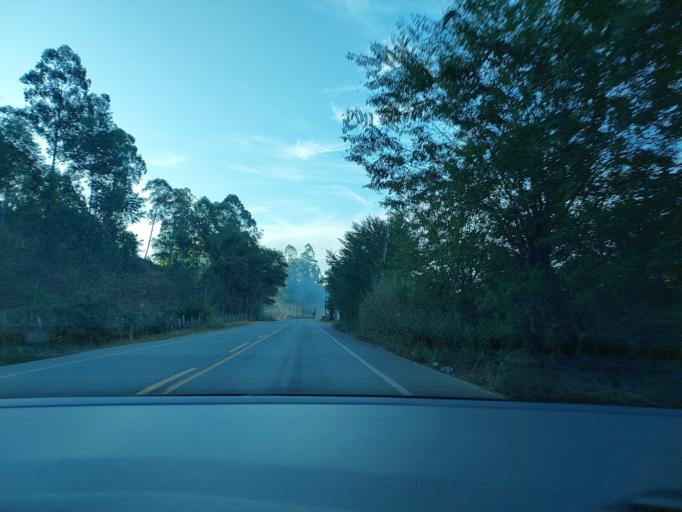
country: BR
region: Minas Gerais
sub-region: Vicosa
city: Vicosa
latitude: -20.8305
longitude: -42.8141
